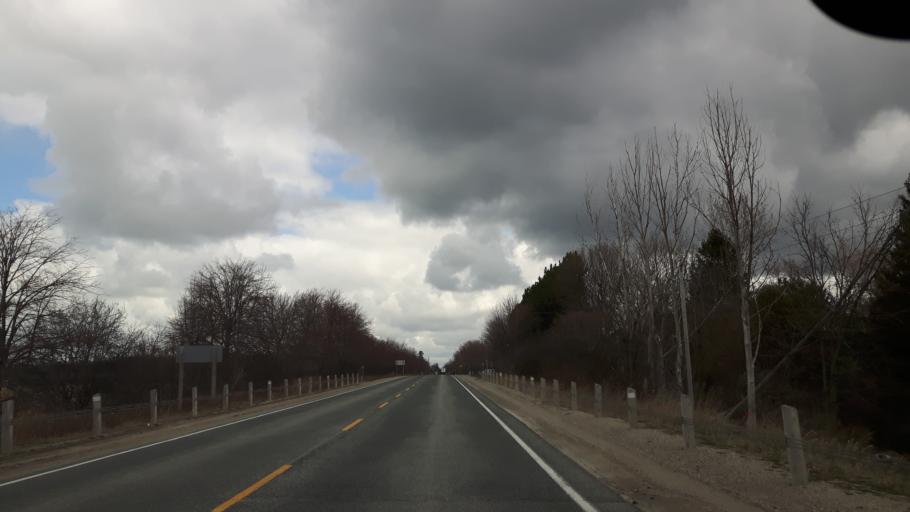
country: CA
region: Ontario
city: Bluewater
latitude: 43.5440
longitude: -81.6905
